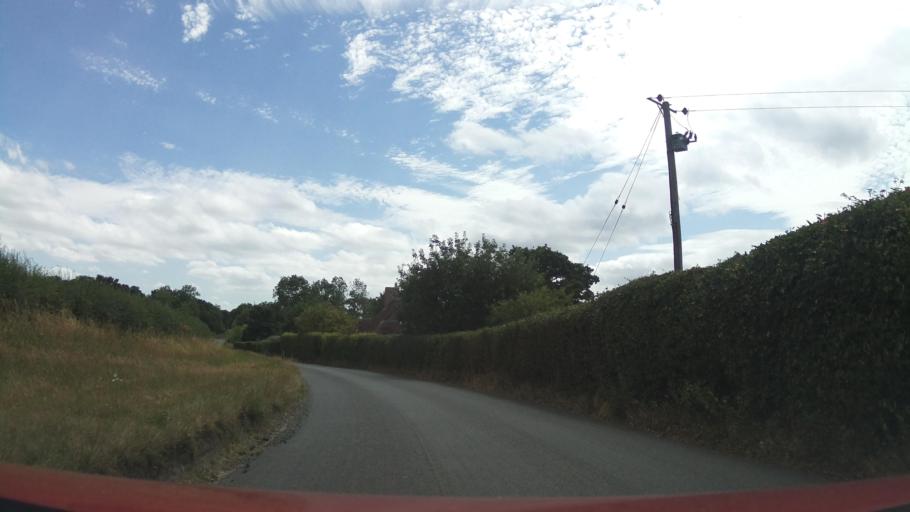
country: GB
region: England
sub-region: Warwickshire
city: Henley in Arden
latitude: 52.2757
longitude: -1.7647
